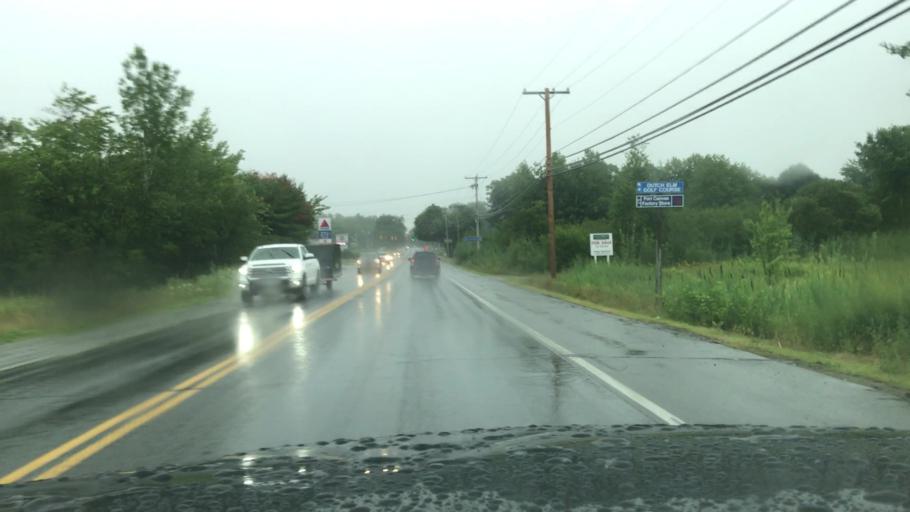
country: US
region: Maine
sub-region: York County
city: Kennebunk
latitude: 43.4056
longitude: -70.5241
